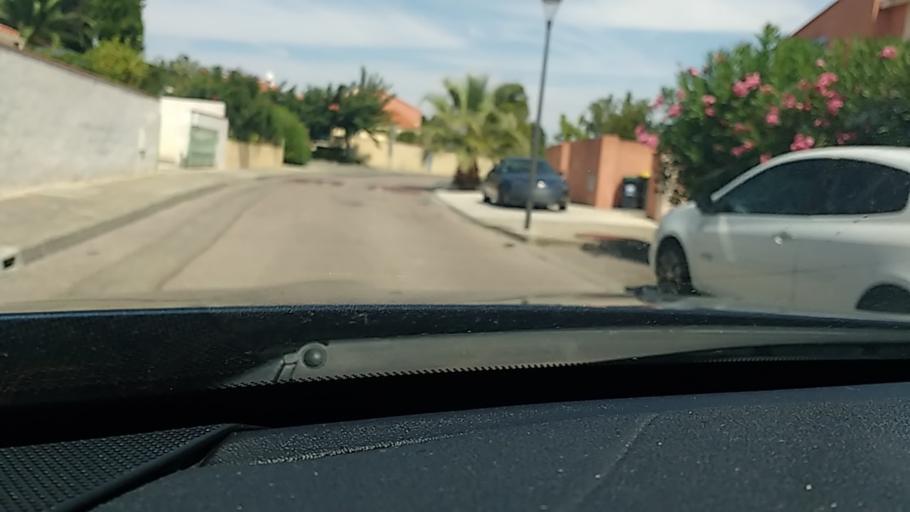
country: FR
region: Languedoc-Roussillon
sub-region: Departement des Pyrenees-Orientales
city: Villeneuve-de-la-Raho
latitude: 42.6332
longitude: 2.9204
